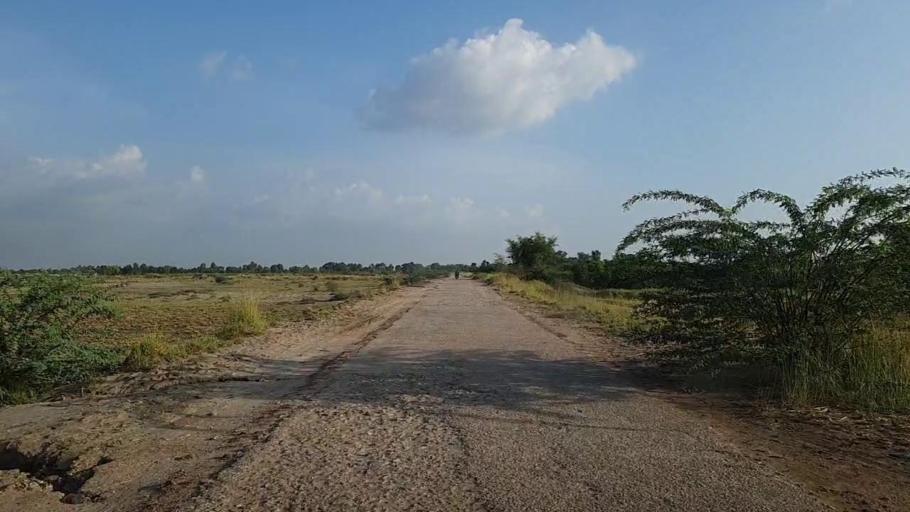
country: PK
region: Sindh
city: Hingorja
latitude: 27.0696
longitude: 68.4188
